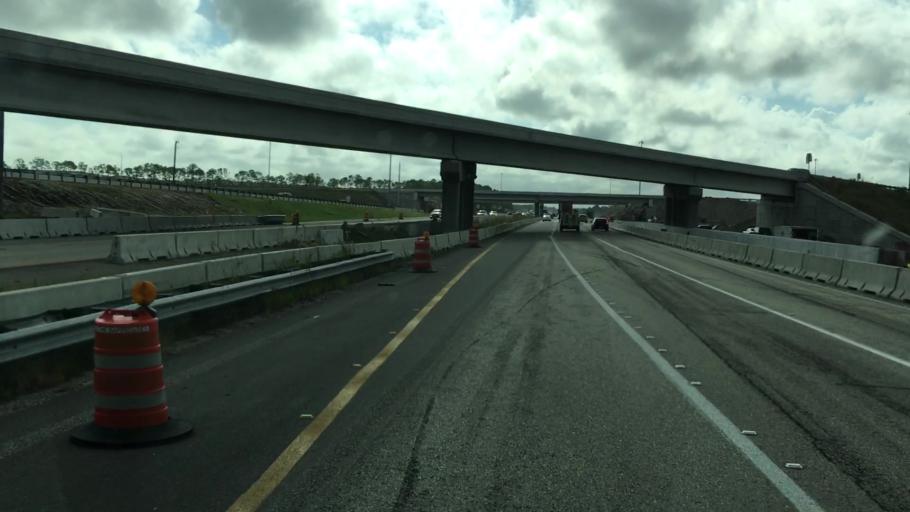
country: US
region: Florida
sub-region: Volusia County
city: South Daytona
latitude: 29.1581
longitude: -81.0773
